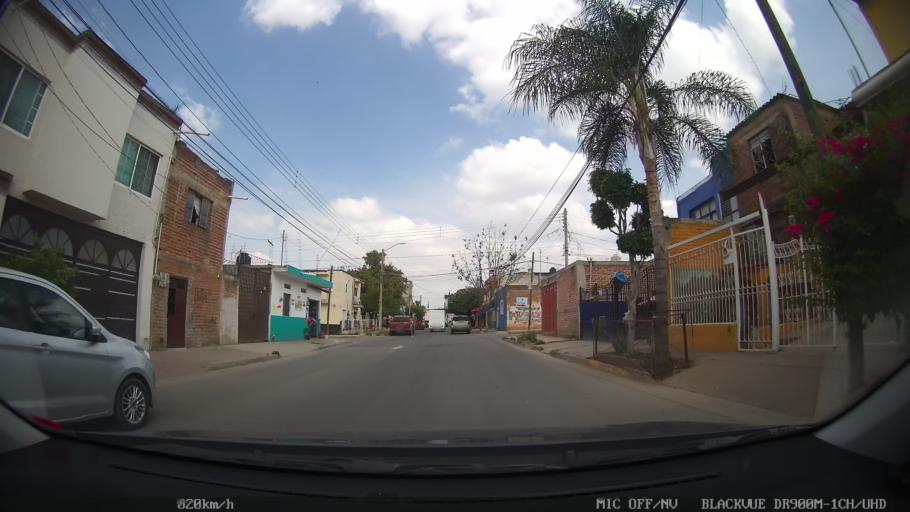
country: MX
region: Jalisco
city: Tonala
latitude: 20.6308
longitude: -103.2352
